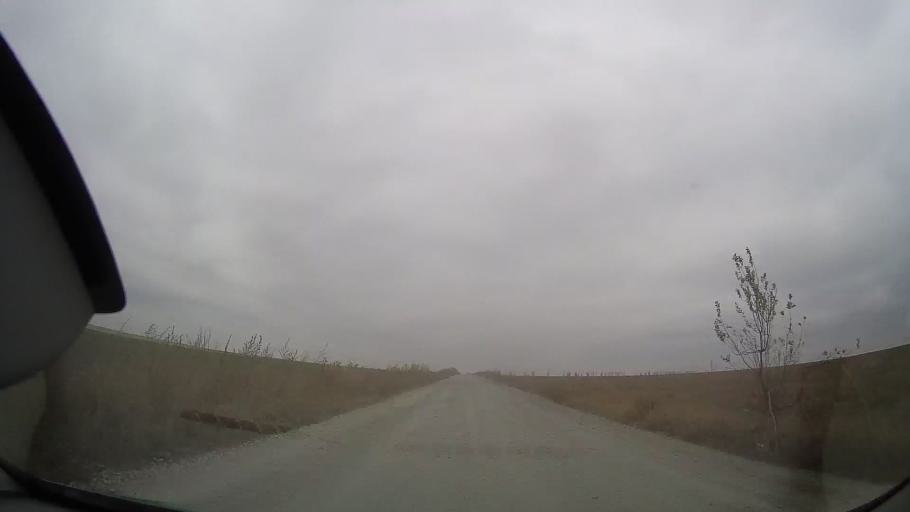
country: RO
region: Ialomita
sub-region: Comuna Grivita
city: Grivita
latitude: 44.7507
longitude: 27.2649
